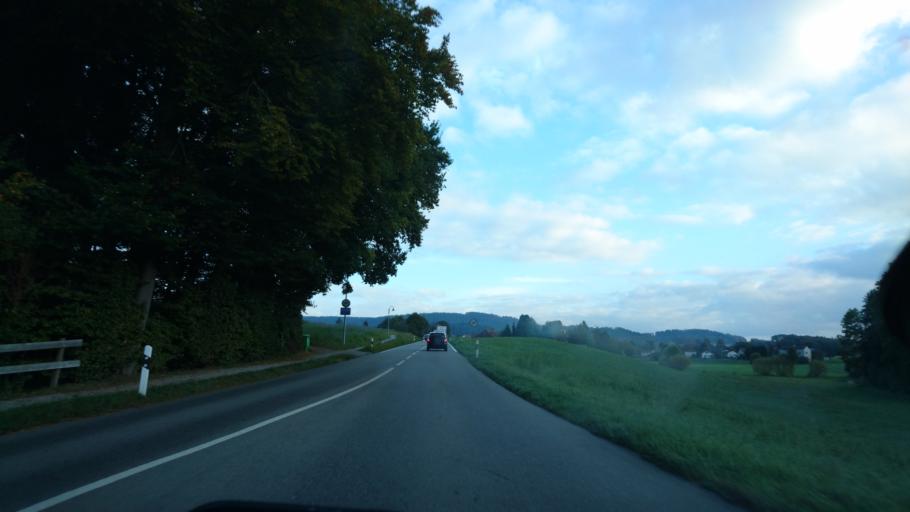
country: CH
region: Bern
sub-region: Bern-Mittelland District
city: Worb
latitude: 46.9230
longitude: 7.5786
